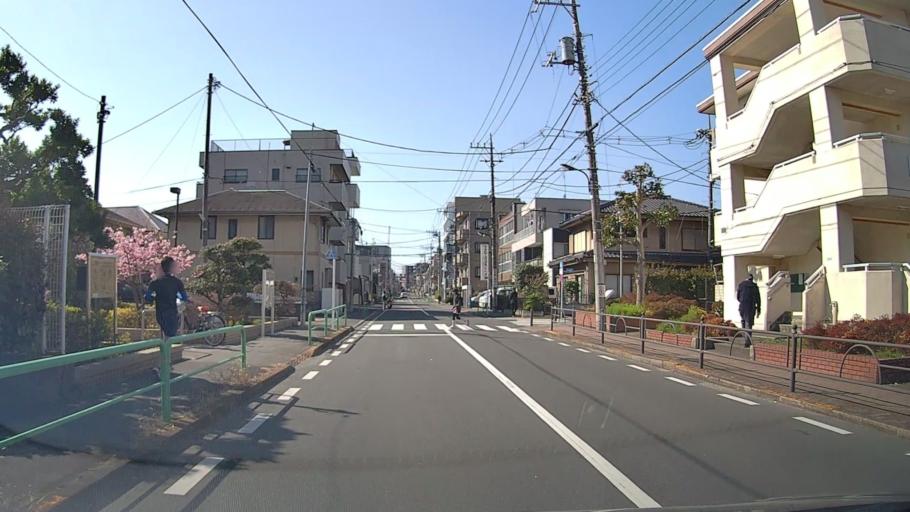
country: JP
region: Tokyo
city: Tokyo
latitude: 35.7316
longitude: 139.6647
